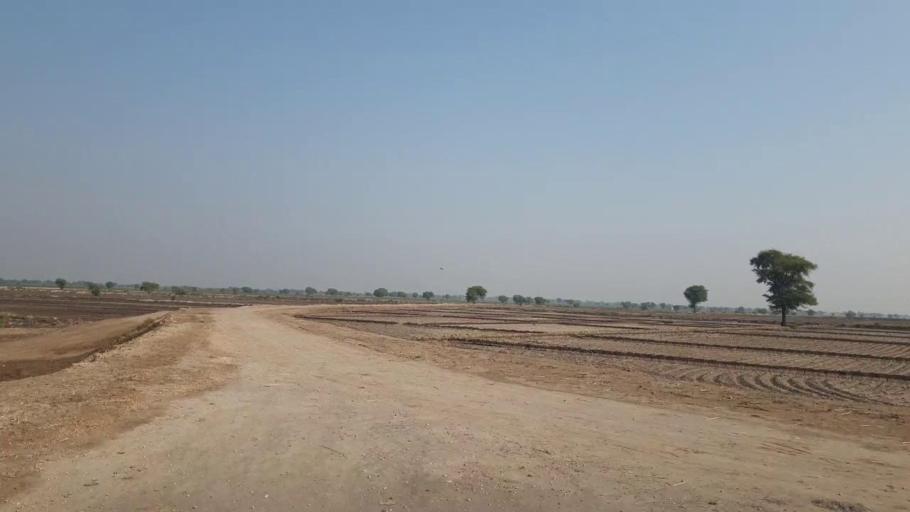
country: PK
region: Sindh
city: Sehwan
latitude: 26.4503
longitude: 67.8286
